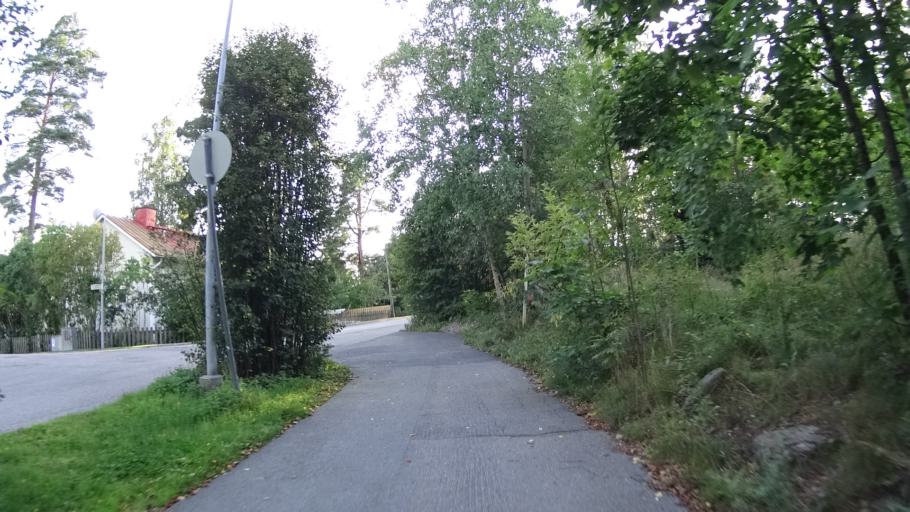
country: FI
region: Uusimaa
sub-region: Helsinki
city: Teekkarikylae
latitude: 60.2432
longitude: 24.8362
